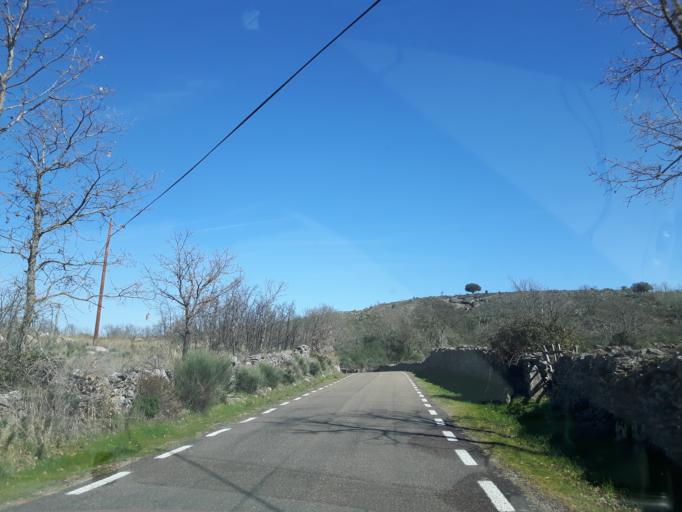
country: ES
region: Castille and Leon
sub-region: Provincia de Salamanca
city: Bermellar
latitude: 40.9747
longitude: -6.6743
